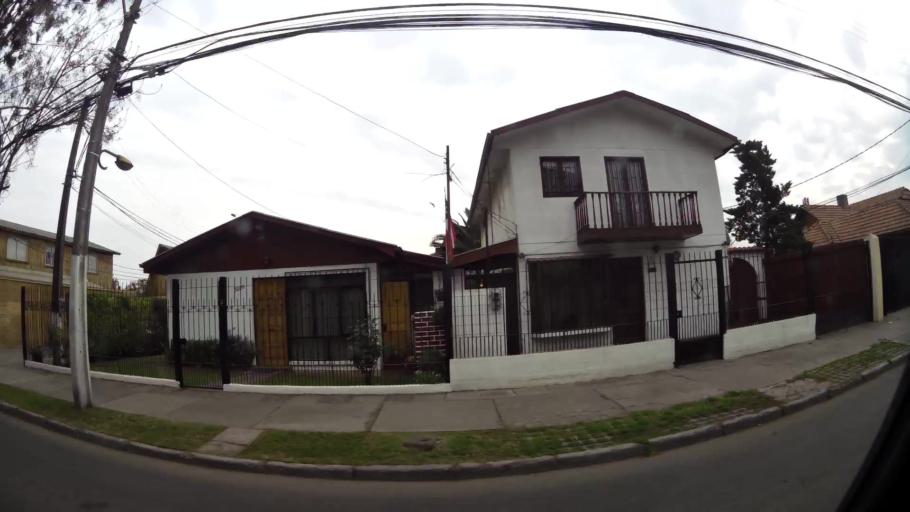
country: CL
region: Santiago Metropolitan
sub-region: Provincia de Santiago
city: Lo Prado
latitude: -33.4981
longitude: -70.7603
